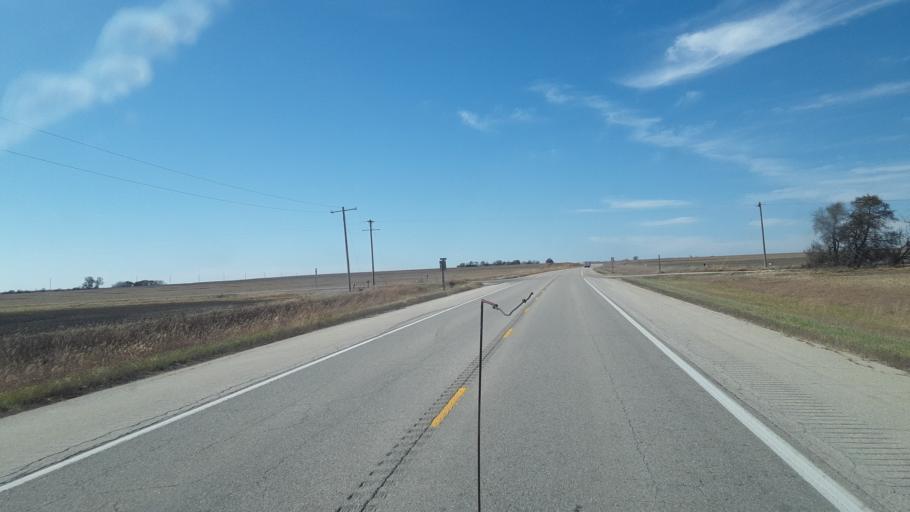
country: US
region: Kansas
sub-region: McPherson County
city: Inman
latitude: 38.3770
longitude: -97.8497
